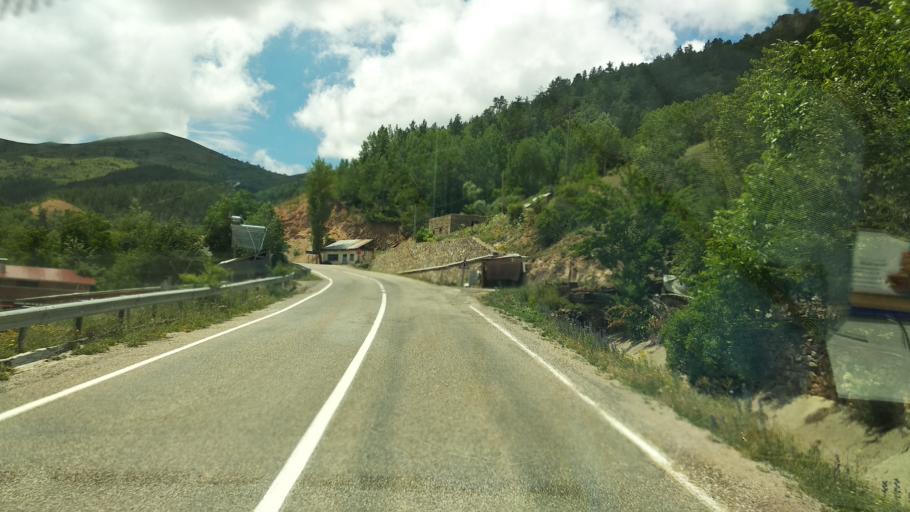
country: TR
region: Gumushane
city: Kose
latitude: 40.3059
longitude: 39.5577
